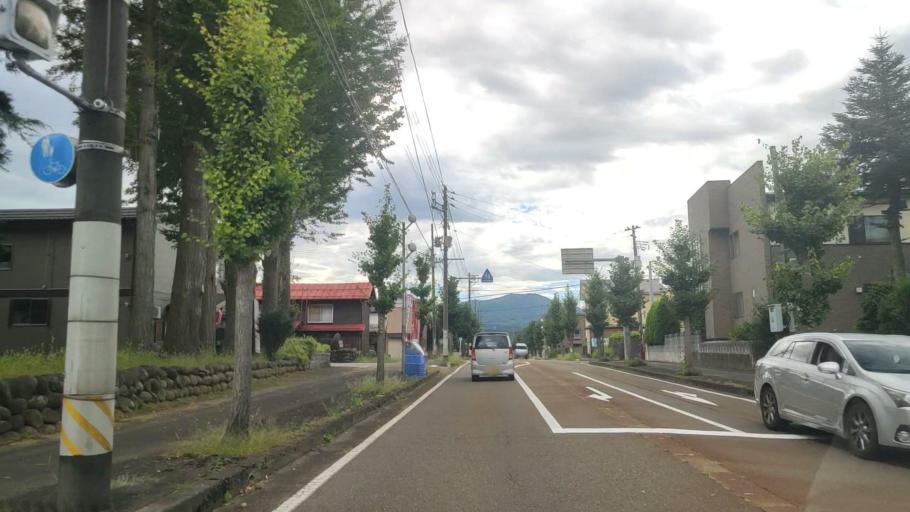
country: JP
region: Niigata
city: Arai
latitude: 37.0250
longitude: 138.2461
